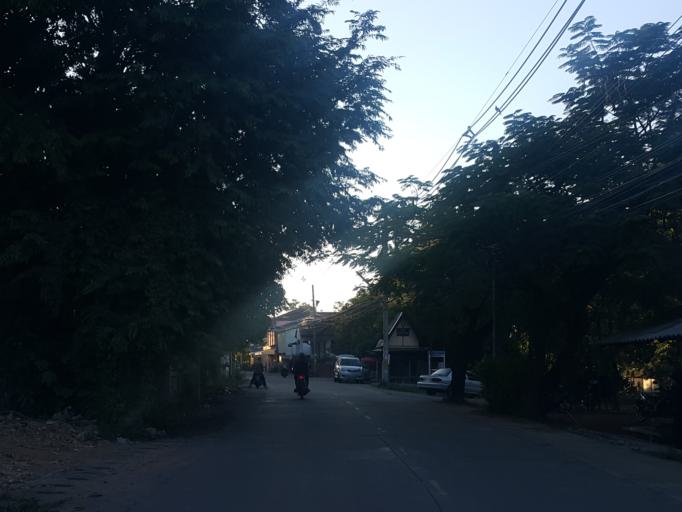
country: TH
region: Chiang Mai
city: San Sai
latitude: 18.8746
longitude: 99.1410
